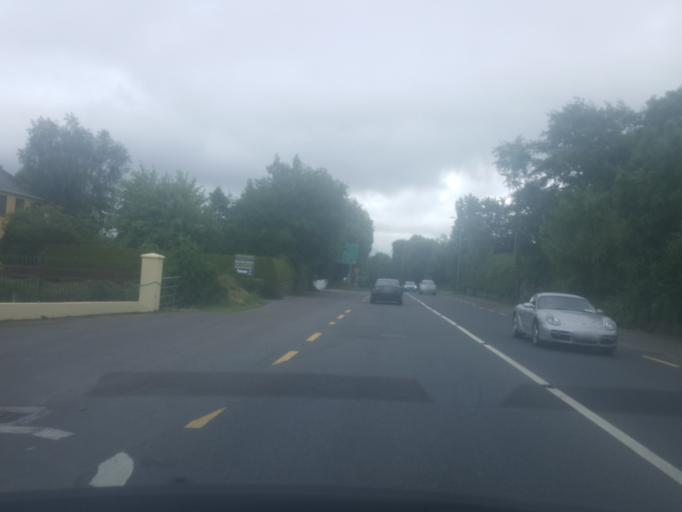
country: IE
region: Munster
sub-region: Ciarrai
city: Cill Airne
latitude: 52.0722
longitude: -9.5208
